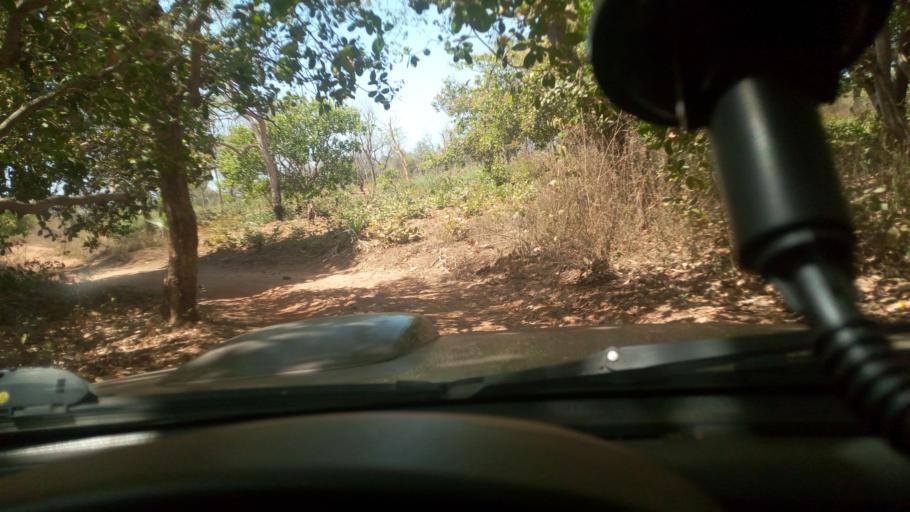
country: GW
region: Oio
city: Farim
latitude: 12.4639
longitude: -15.3555
